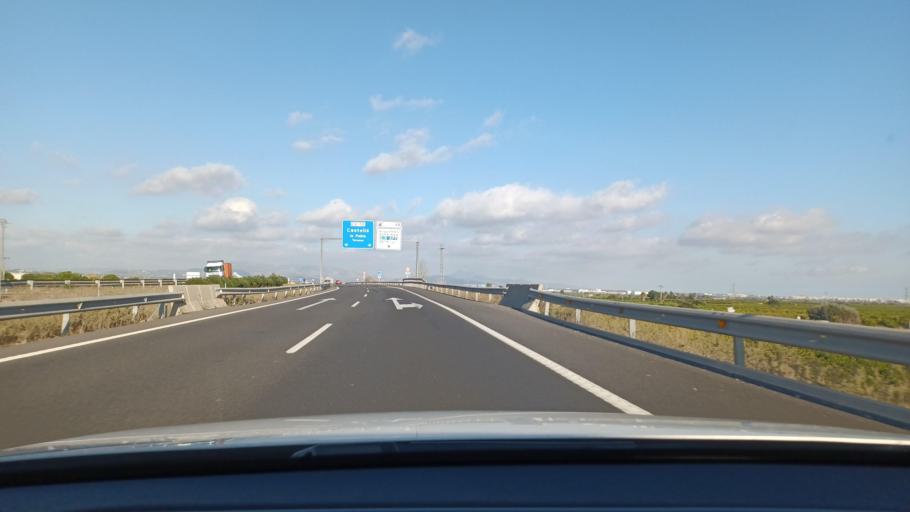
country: ES
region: Valencia
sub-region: Provincia de Castello
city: Betxi
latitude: 39.9230
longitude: -0.1933
